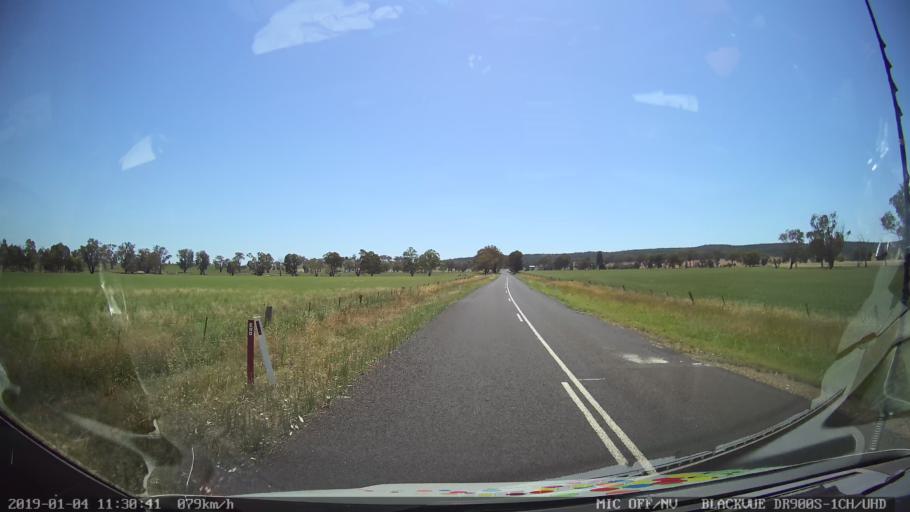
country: AU
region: New South Wales
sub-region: Cabonne
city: Molong
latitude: -33.0760
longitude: 148.7838
